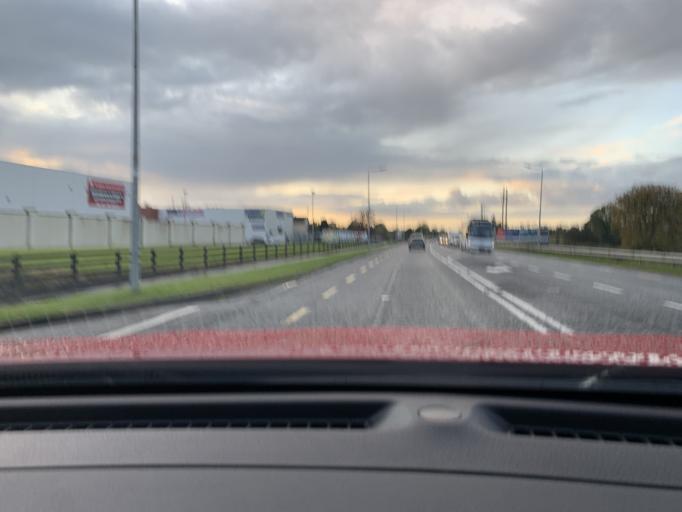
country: IE
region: Connaught
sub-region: County Leitrim
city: Carrick-on-Shannon
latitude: 53.9426
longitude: -8.1084
